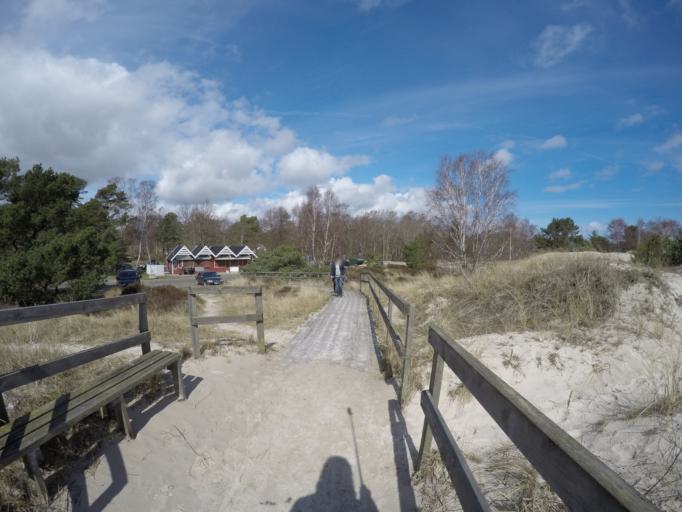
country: SE
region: Skane
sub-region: Simrishamns Kommun
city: Simrishamn
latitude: 55.3857
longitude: 14.1959
